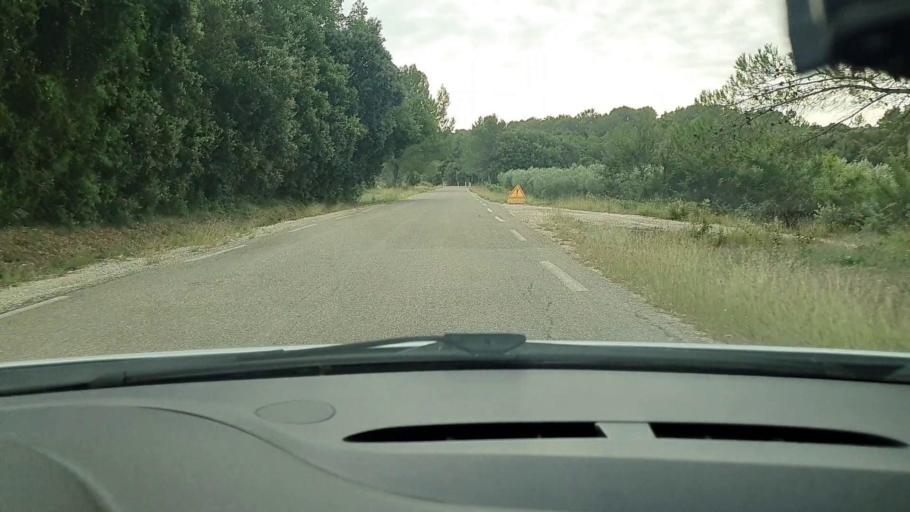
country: FR
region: Languedoc-Roussillon
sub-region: Departement du Gard
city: Montaren-et-Saint-Mediers
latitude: 44.0559
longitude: 4.3273
